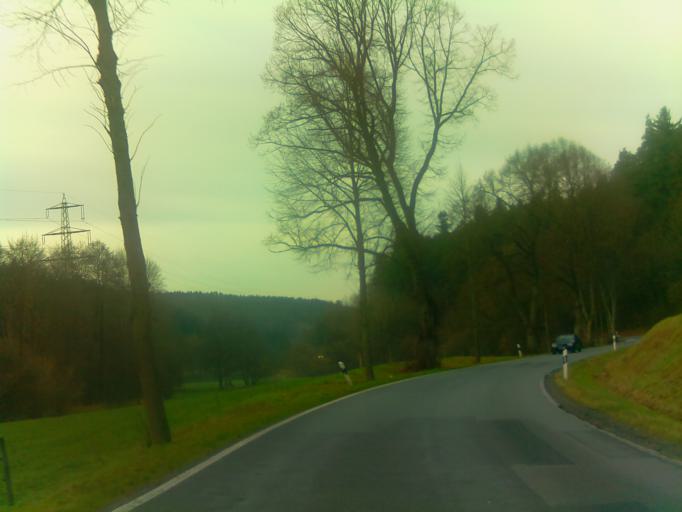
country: DE
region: Hesse
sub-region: Regierungsbezirk Darmstadt
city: Erbach
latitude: 49.6252
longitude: 8.9430
